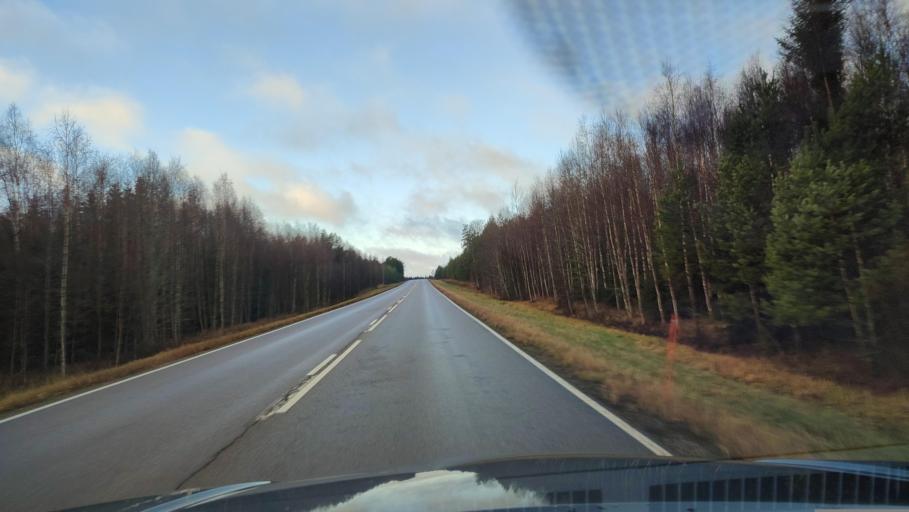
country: FI
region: Ostrobothnia
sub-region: Sydosterbotten
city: Kristinestad
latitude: 62.3010
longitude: 21.4064
